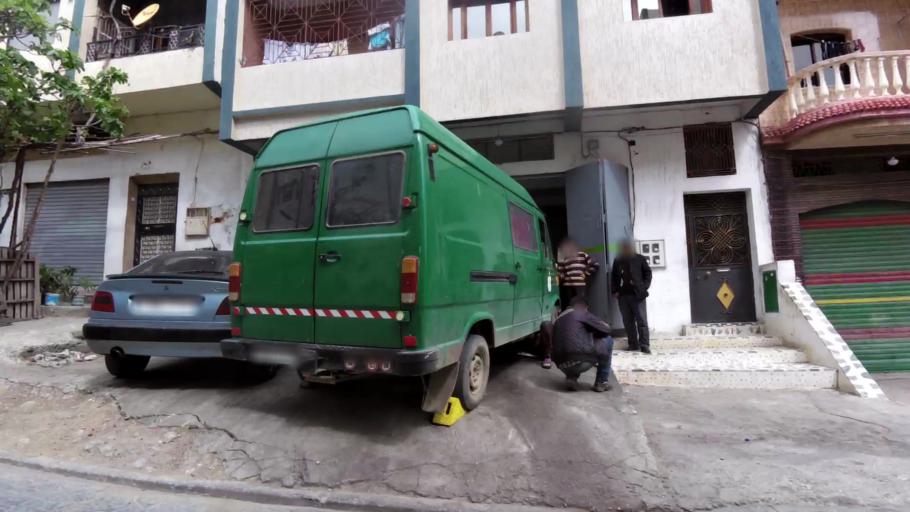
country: MA
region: Tanger-Tetouan
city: Tetouan
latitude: 35.5693
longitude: -5.3945
